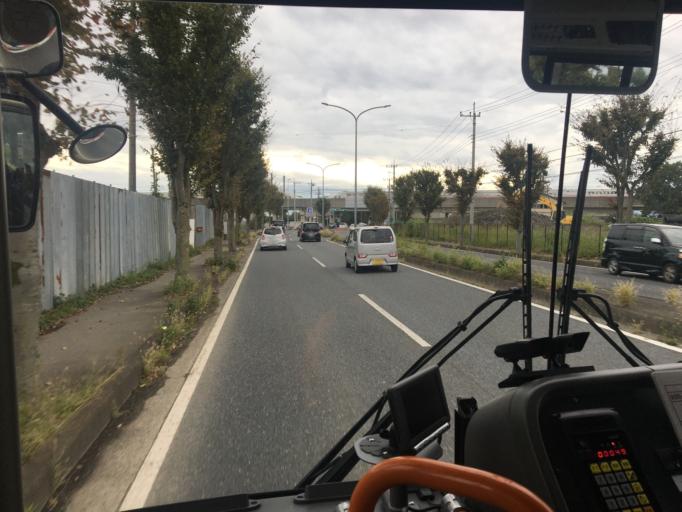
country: JP
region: Saitama
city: Fukiage-fujimi
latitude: 36.1136
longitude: 139.4600
